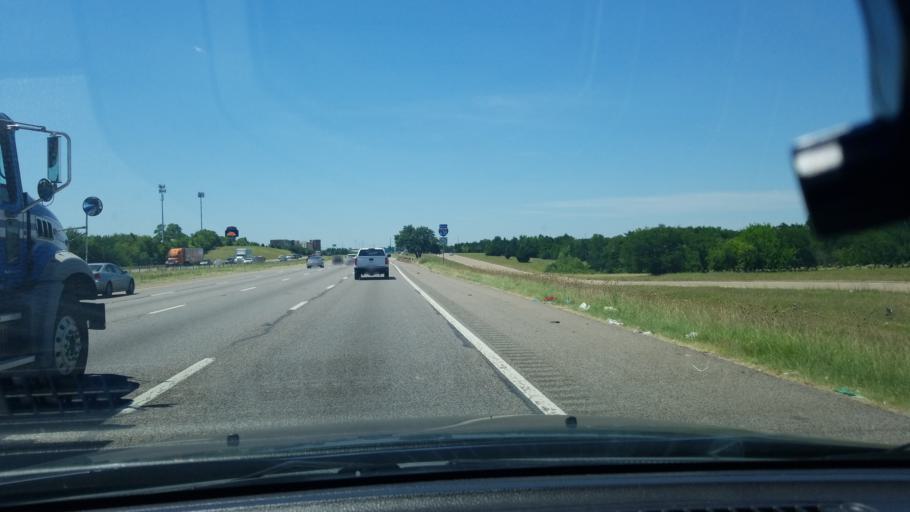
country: US
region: Texas
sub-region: Dallas County
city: Mesquite
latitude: 32.7575
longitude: -96.6178
